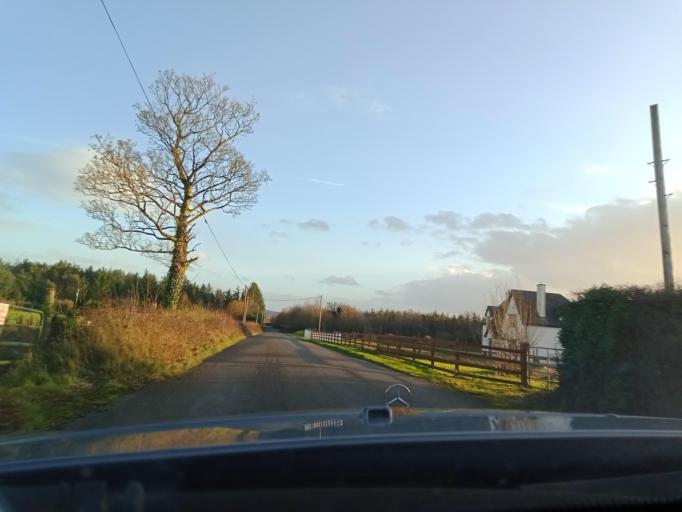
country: IE
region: Leinster
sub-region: Kilkenny
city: Callan
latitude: 52.4990
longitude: -7.3386
